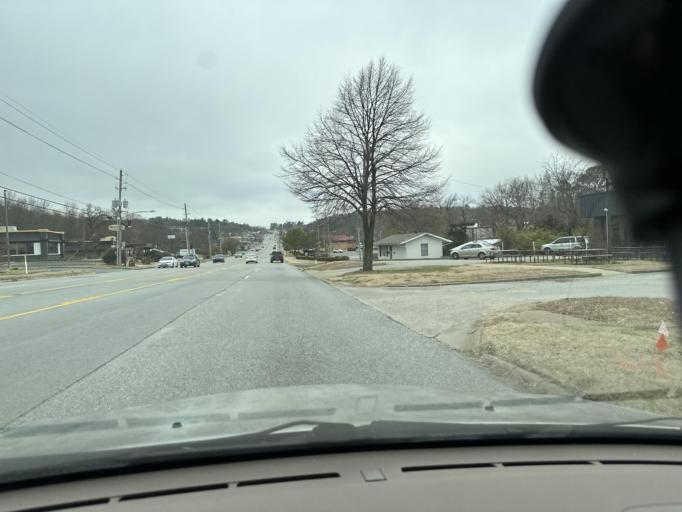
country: US
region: Arkansas
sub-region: Washington County
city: Fayetteville
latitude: 36.0907
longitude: -94.1540
